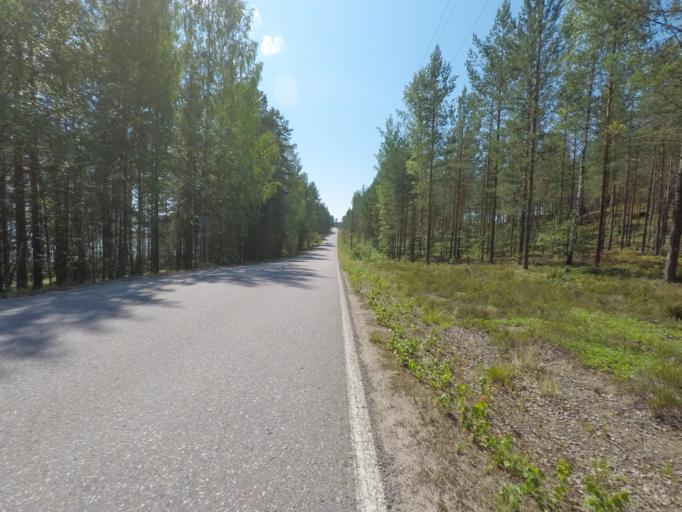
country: FI
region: Southern Savonia
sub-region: Mikkeli
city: Puumala
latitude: 61.4591
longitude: 28.1750
